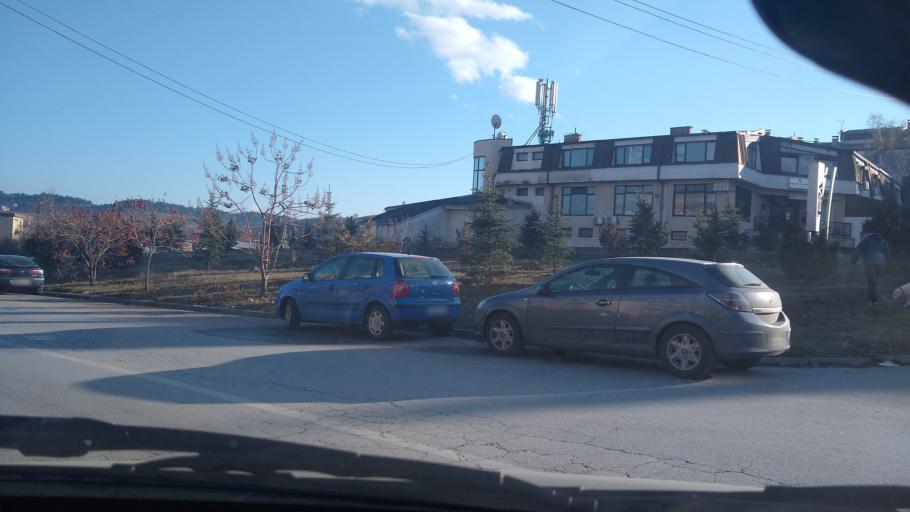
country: MK
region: Bitola
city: Bitola
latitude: 41.0231
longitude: 21.3148
